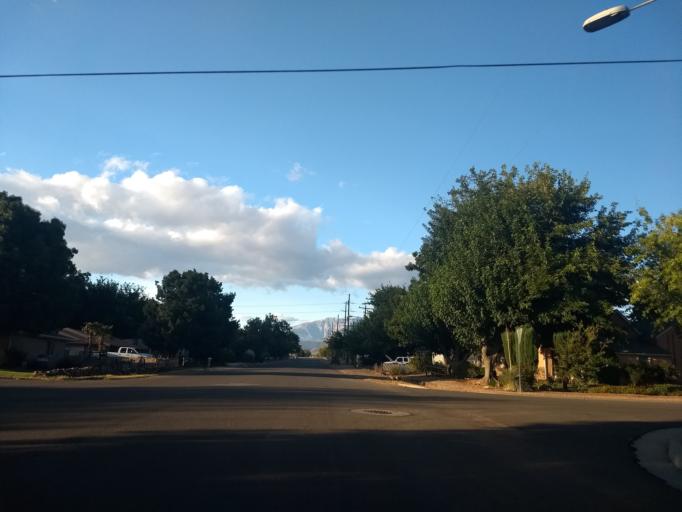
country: US
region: Utah
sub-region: Washington County
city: Washington
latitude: 37.1262
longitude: -113.5099
